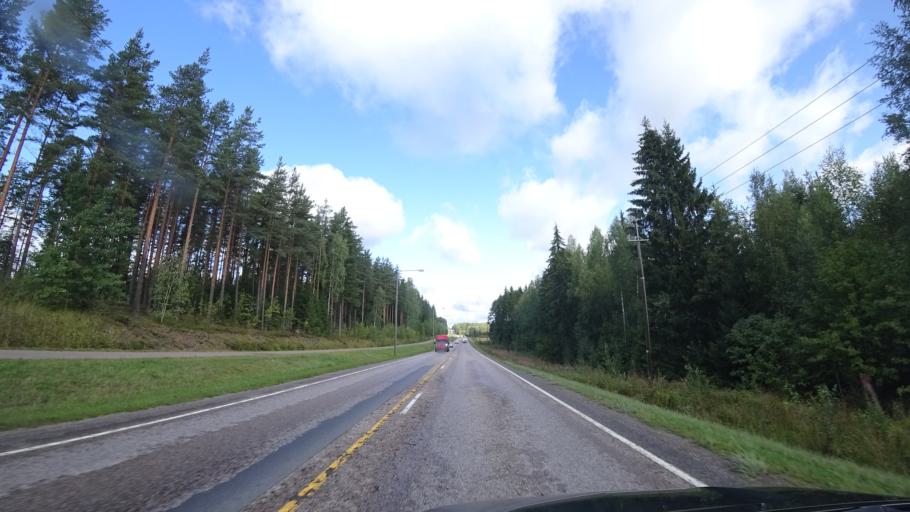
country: FI
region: Uusimaa
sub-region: Helsinki
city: Tuusula
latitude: 60.4303
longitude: 24.9926
